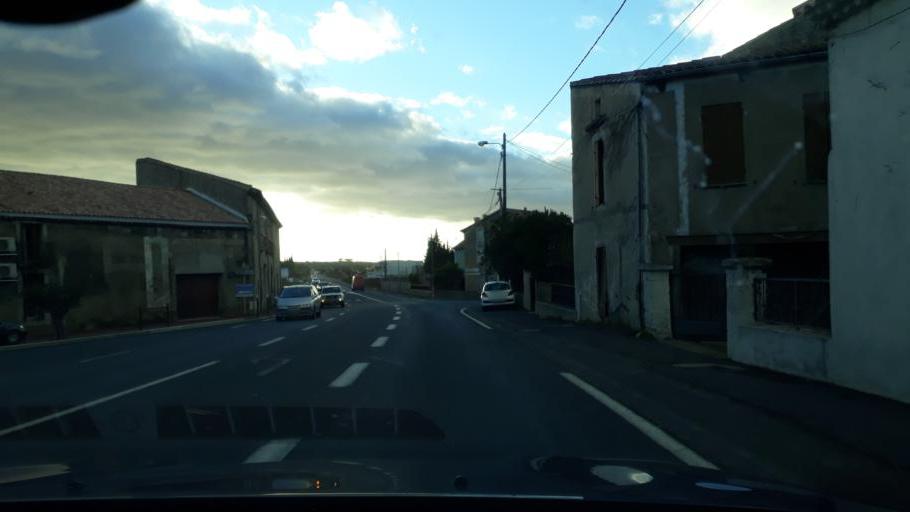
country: FR
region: Languedoc-Roussillon
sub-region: Departement de l'Herault
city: Nissan-lez-Enserune
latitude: 43.2920
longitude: 3.1211
